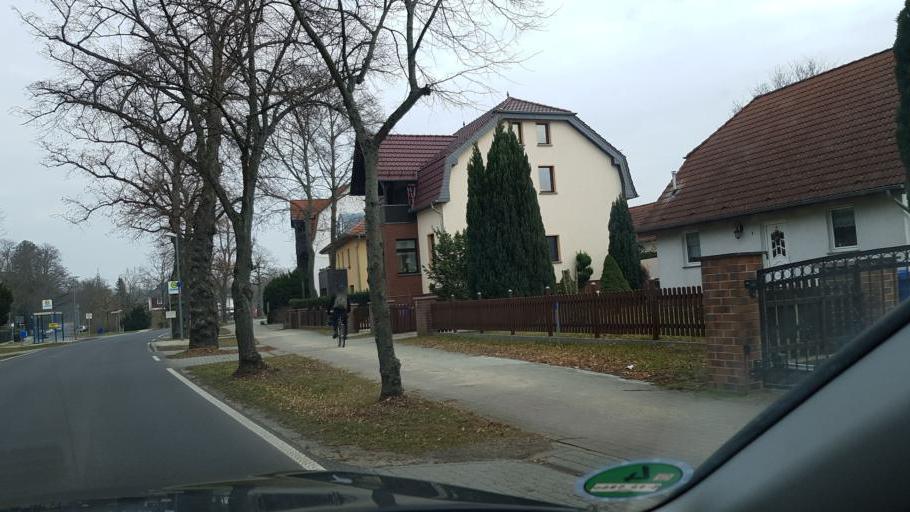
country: DE
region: Brandenburg
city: Konigs Wusterhausen
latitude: 52.2980
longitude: 13.6535
